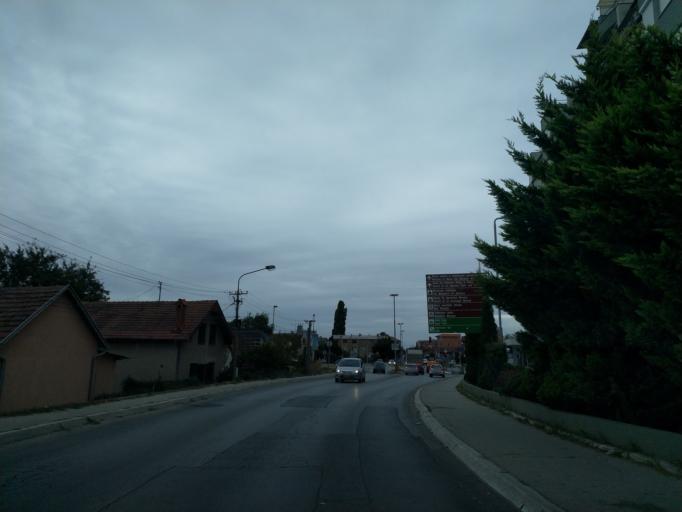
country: RS
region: Central Serbia
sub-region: Pomoravski Okrug
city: Jagodina
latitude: 43.9865
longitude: 21.2487
